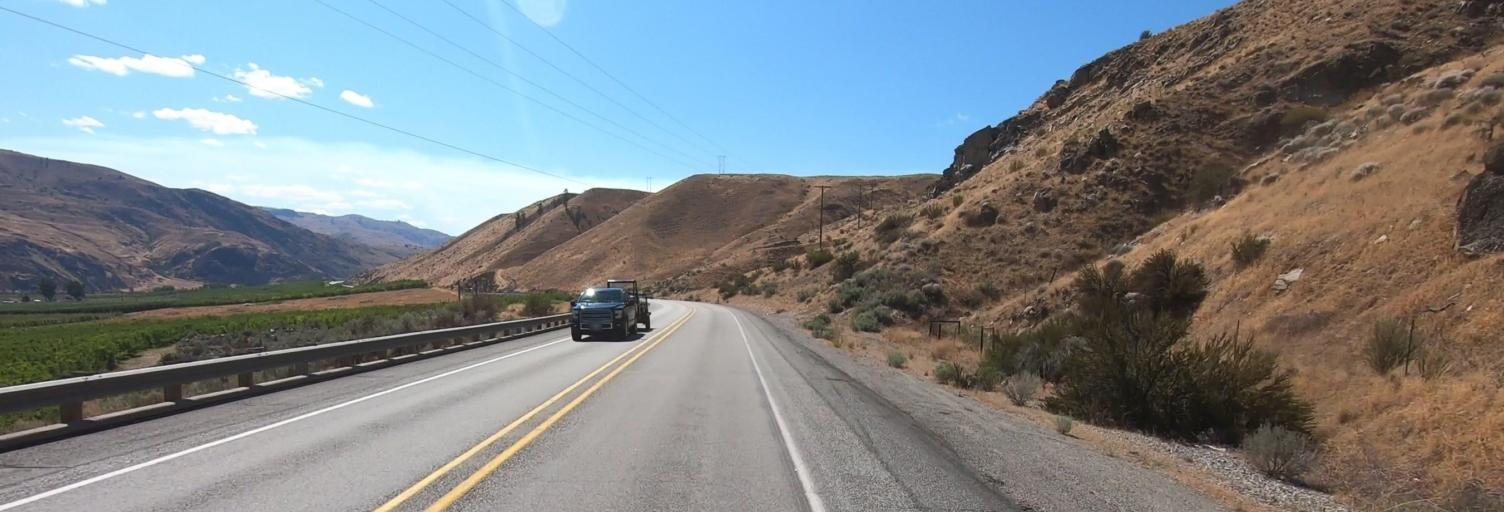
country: US
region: Washington
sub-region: Chelan County
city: Chelan
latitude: 47.9449
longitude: -119.8829
